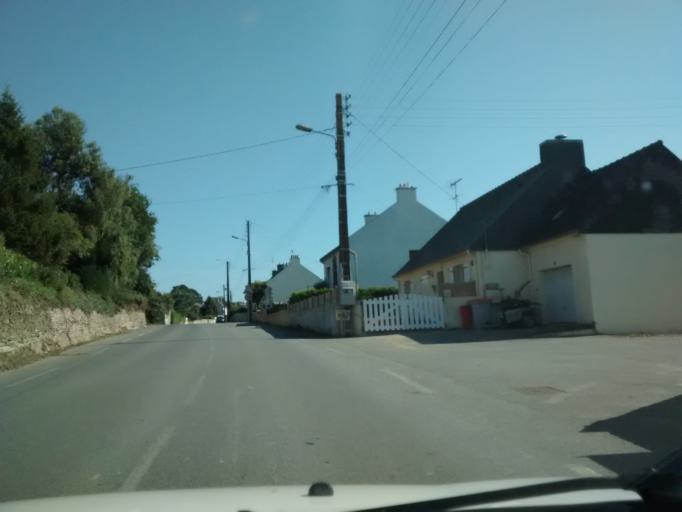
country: FR
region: Brittany
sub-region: Departement des Cotes-d'Armor
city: Tredarzec
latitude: 48.7847
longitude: -3.2033
